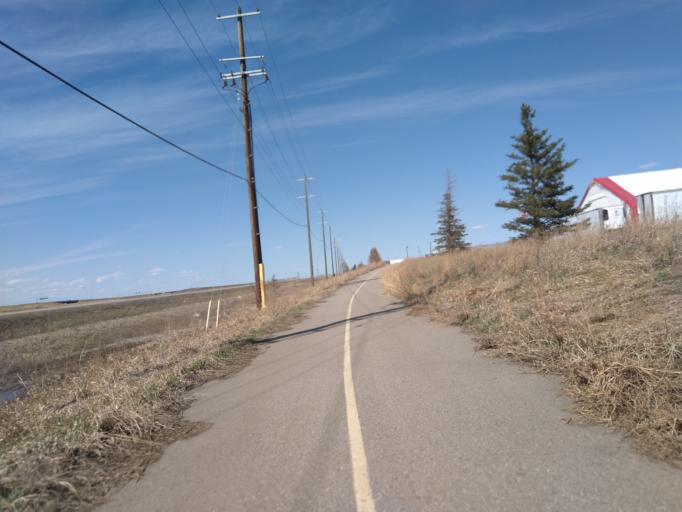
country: CA
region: Alberta
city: Chestermere
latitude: 50.9633
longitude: -113.9116
